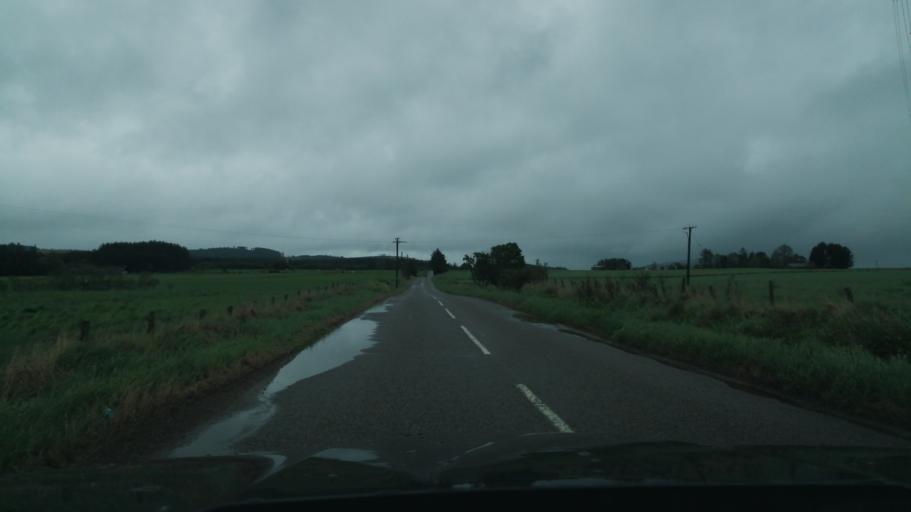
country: GB
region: Scotland
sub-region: Aberdeenshire
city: Huntly
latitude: 57.5405
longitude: -2.7857
